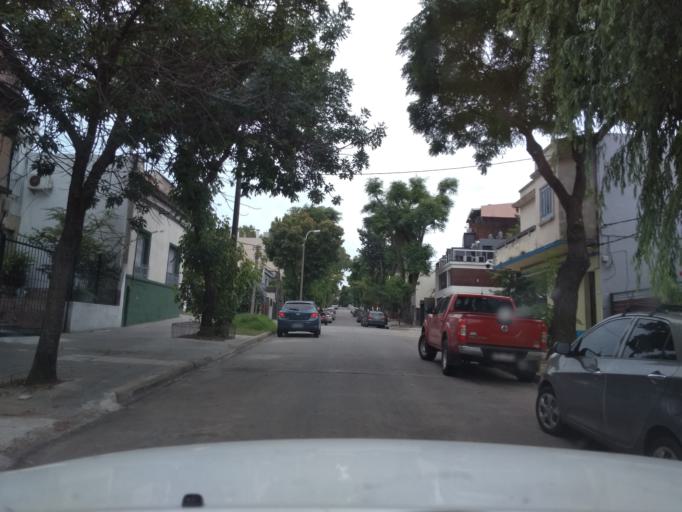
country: UY
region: Montevideo
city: Montevideo
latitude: -34.9049
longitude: -56.1416
